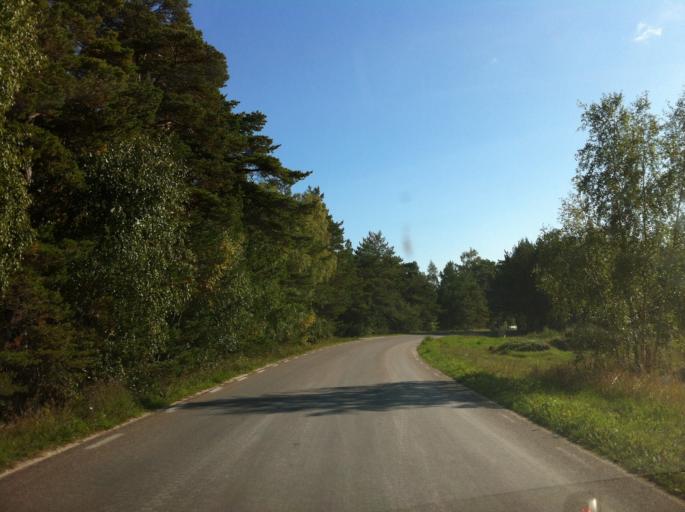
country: SE
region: Gotland
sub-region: Gotland
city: Slite
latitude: 57.9665
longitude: 19.2361
